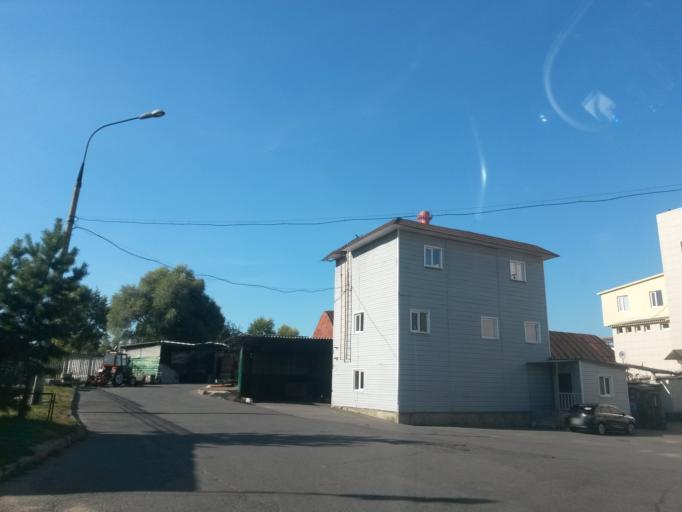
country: RU
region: Moscow
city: Yasenevo
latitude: 55.6100
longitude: 37.5130
